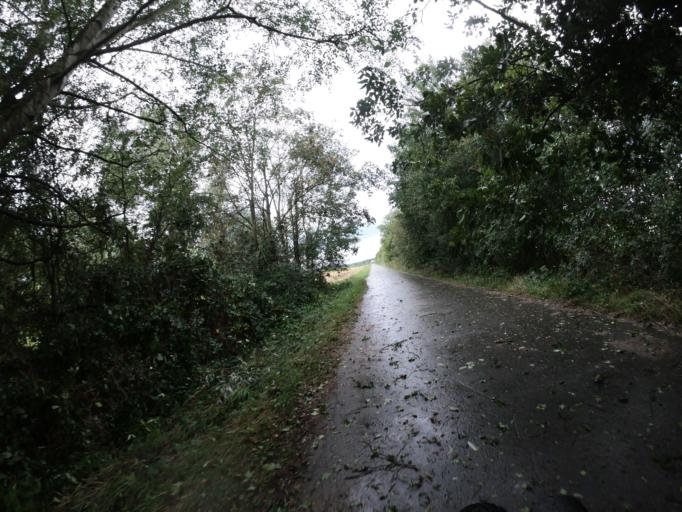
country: DE
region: Hesse
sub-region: Regierungsbezirk Darmstadt
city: Erzhausen
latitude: 49.9593
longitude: 8.6577
